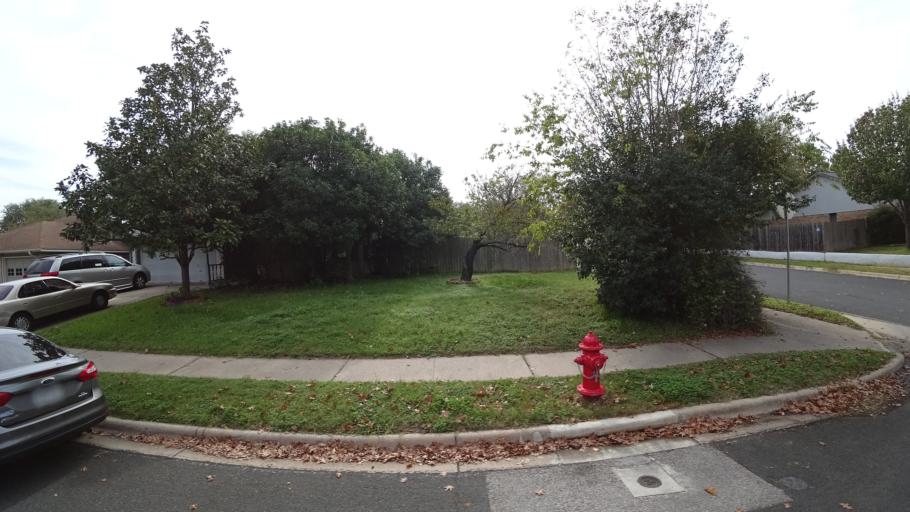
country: US
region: Texas
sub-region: Travis County
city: Wells Branch
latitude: 30.4448
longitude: -97.6831
